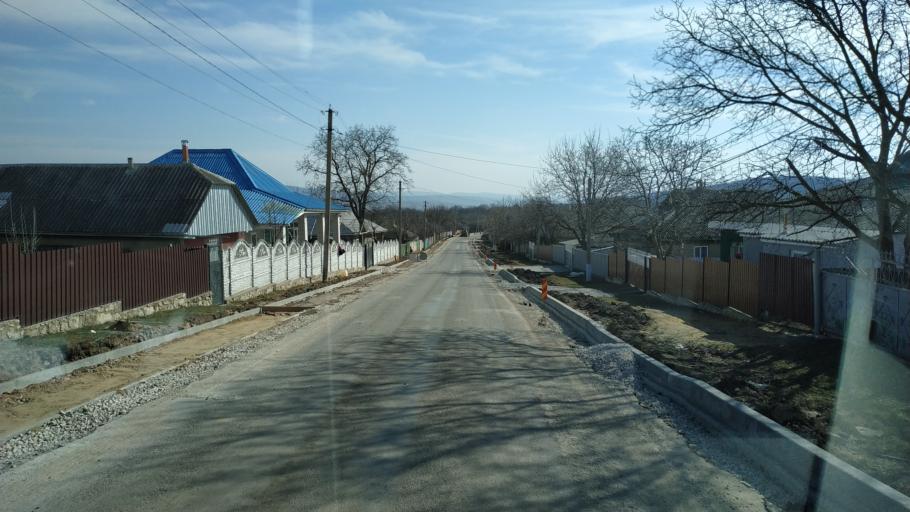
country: MD
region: Nisporeni
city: Nisporeni
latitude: 47.1989
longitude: 28.0628
